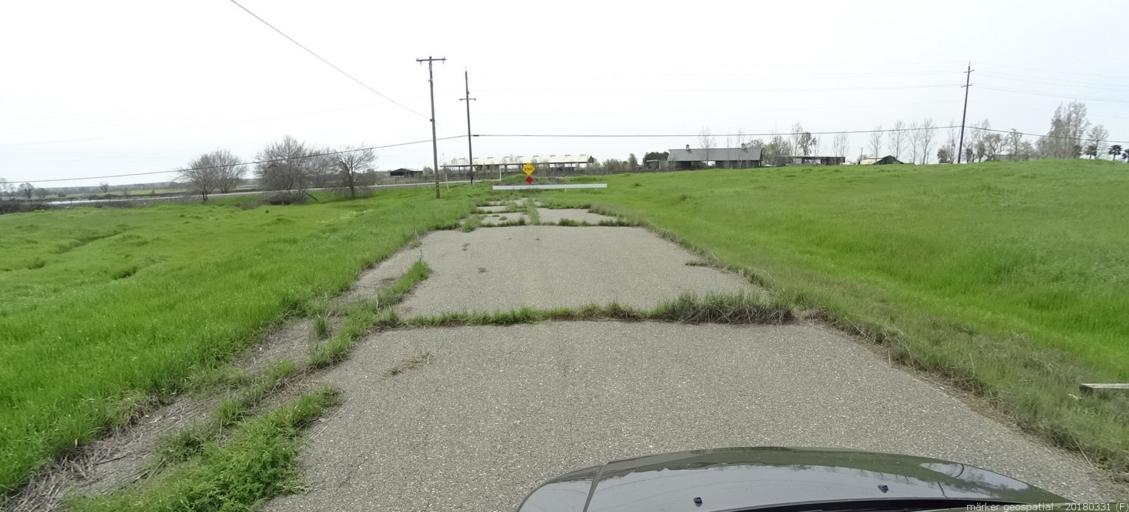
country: US
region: California
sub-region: Sacramento County
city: Rancho Murieta
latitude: 38.4972
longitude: -121.1198
